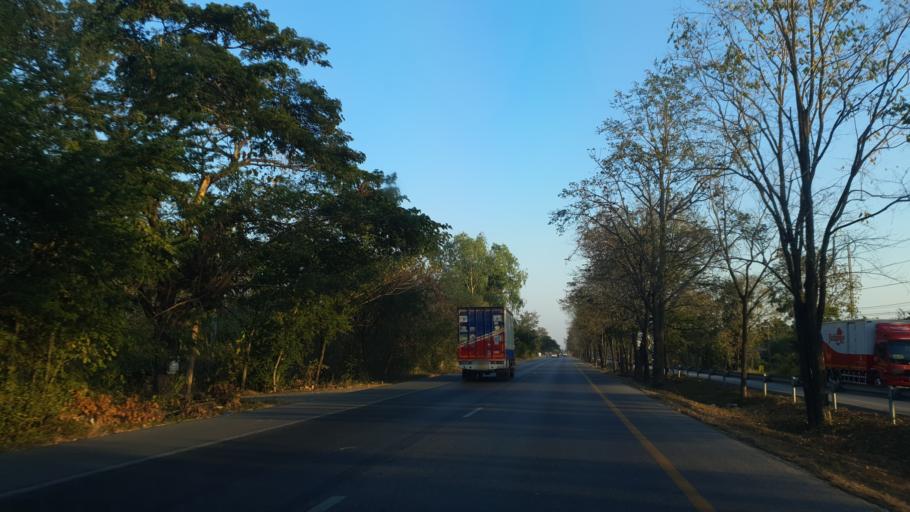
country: TH
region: Kamphaeng Phet
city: Khanu Woralaksaburi
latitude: 16.0345
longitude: 99.7684
